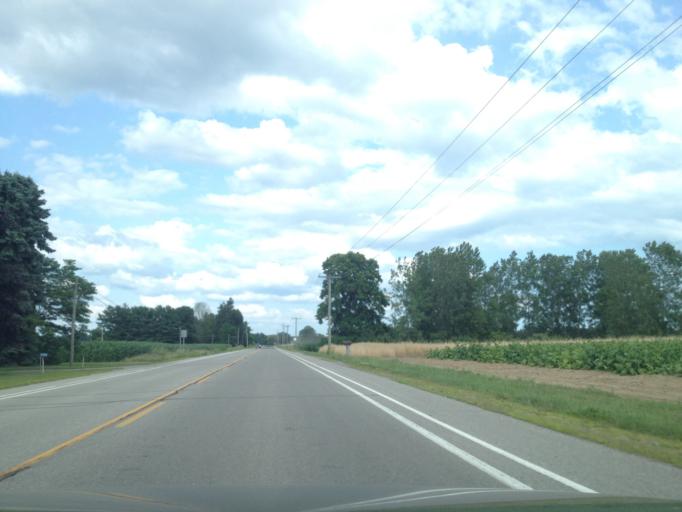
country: CA
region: Ontario
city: Aylmer
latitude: 42.6628
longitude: -81.0029
